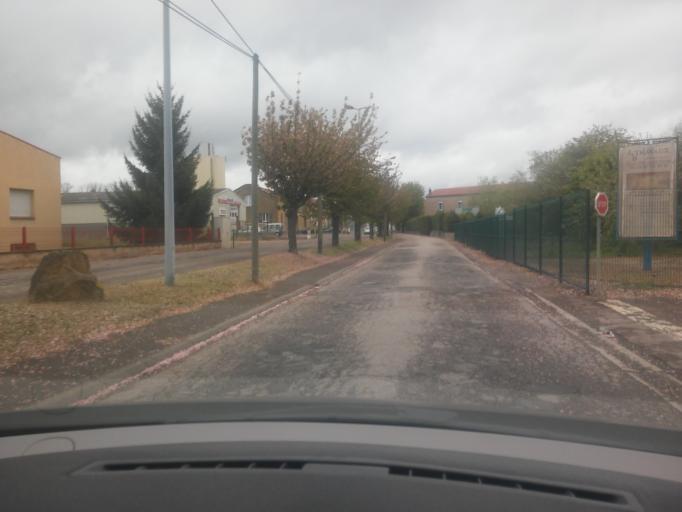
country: FR
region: Lorraine
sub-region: Departement de la Moselle
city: Boulay-Moselle
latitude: 49.1813
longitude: 6.4882
